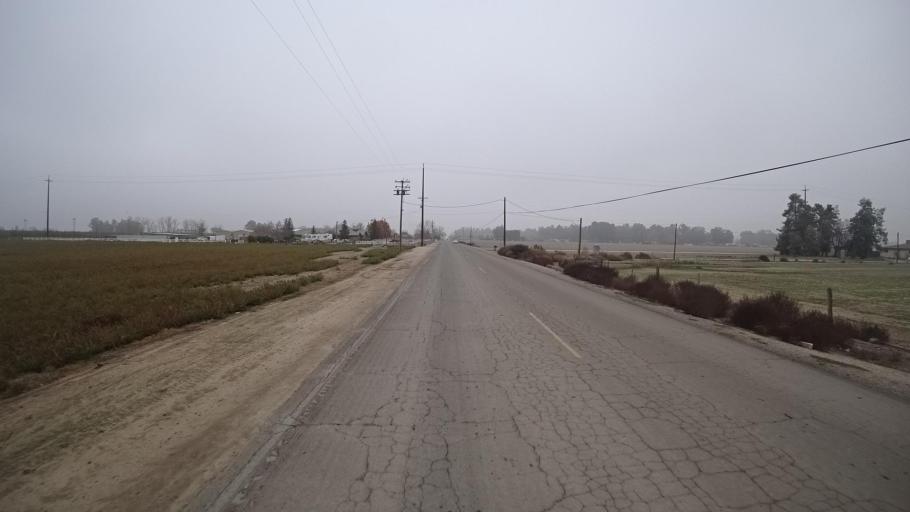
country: US
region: California
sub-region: Kern County
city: Greenfield
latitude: 35.2380
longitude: -119.0975
